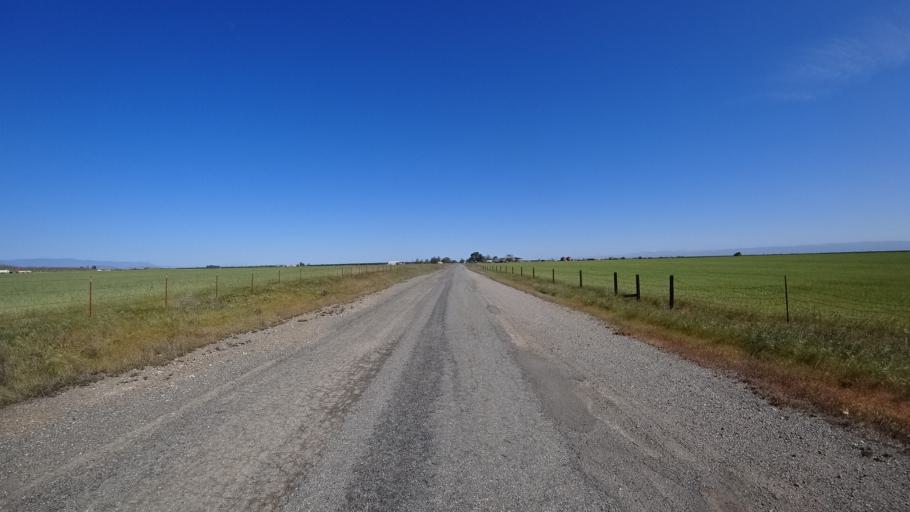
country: US
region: California
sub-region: Glenn County
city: Orland
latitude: 39.6385
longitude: -122.1599
